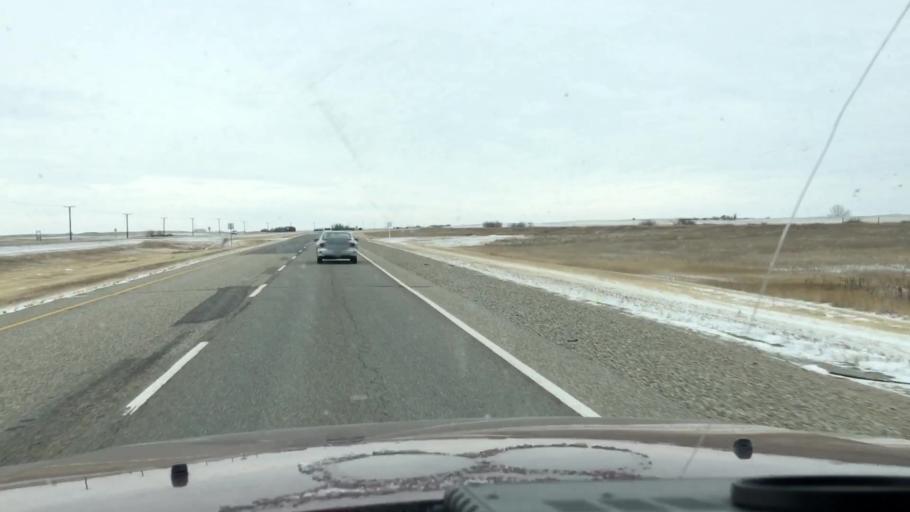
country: CA
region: Saskatchewan
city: Watrous
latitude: 51.4404
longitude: -106.2089
